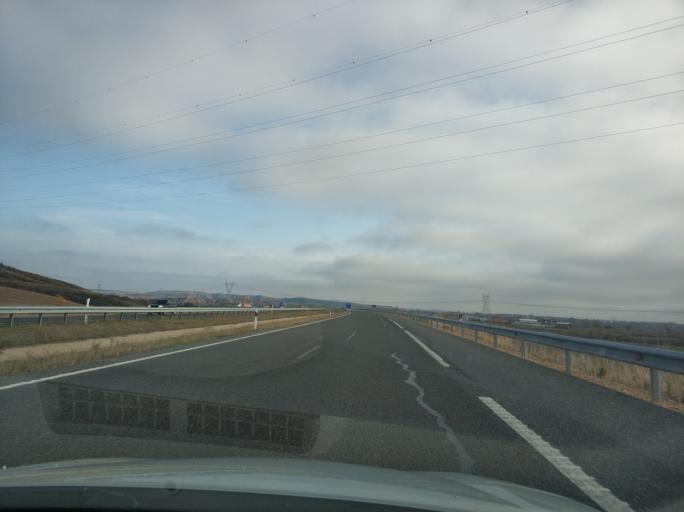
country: ES
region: Castille and Leon
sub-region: Provincia de Leon
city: Valdefresno
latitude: 42.5592
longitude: -5.4736
